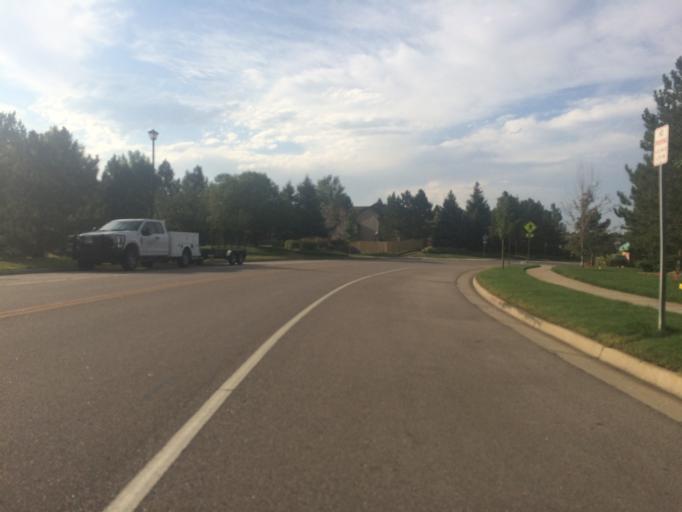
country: US
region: Colorado
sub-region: Boulder County
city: Superior
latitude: 39.9276
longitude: -105.1527
